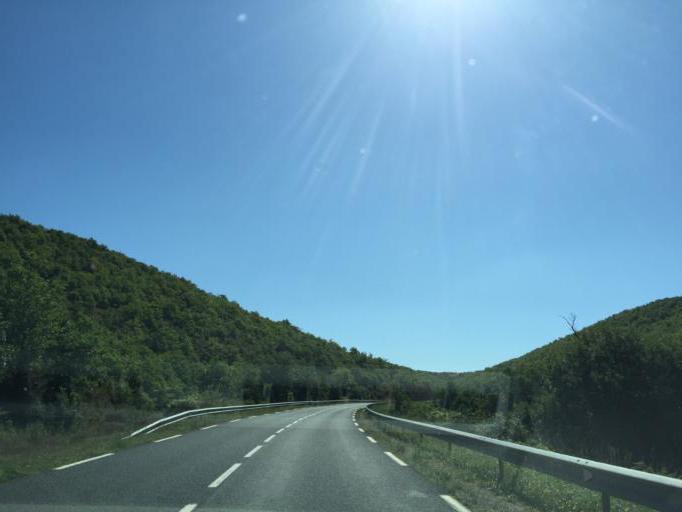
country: FR
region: Midi-Pyrenees
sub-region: Departement de l'Aveyron
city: Saint-Georges-de-Luzencon
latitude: 44.0314
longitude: 2.9243
